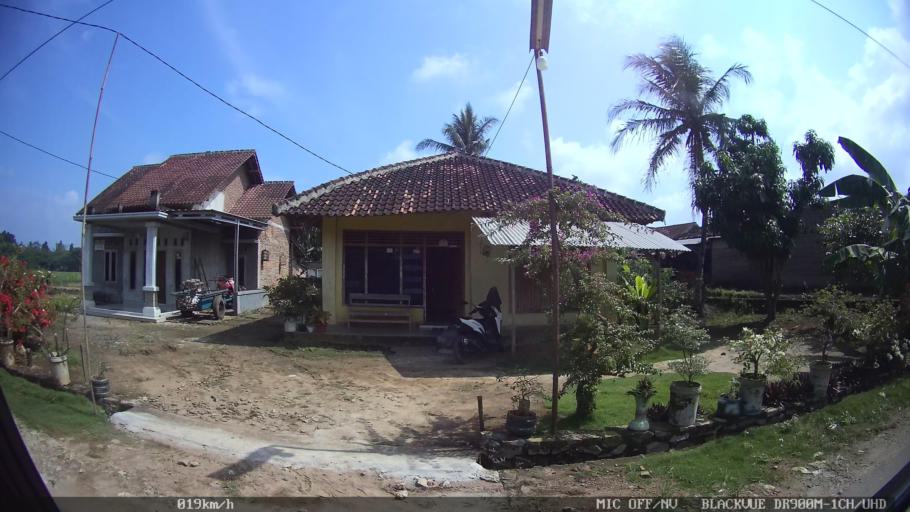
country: ID
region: Lampung
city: Kedaton
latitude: -5.3288
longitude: 105.2752
